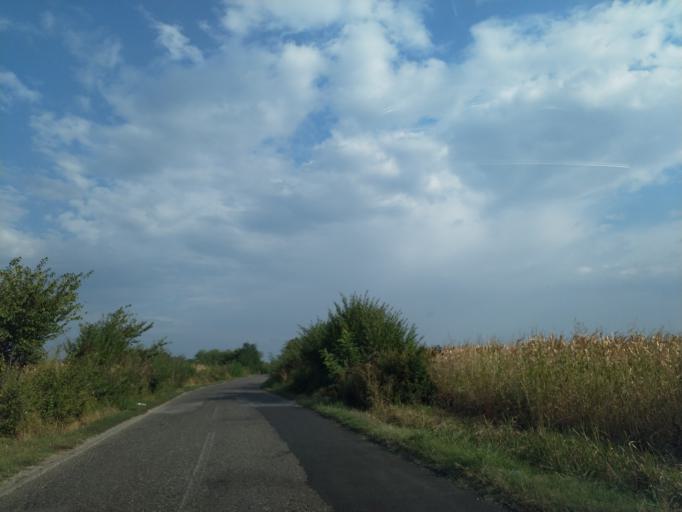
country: RS
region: Central Serbia
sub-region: Pomoravski Okrug
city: Paracin
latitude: 43.8467
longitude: 21.4666
